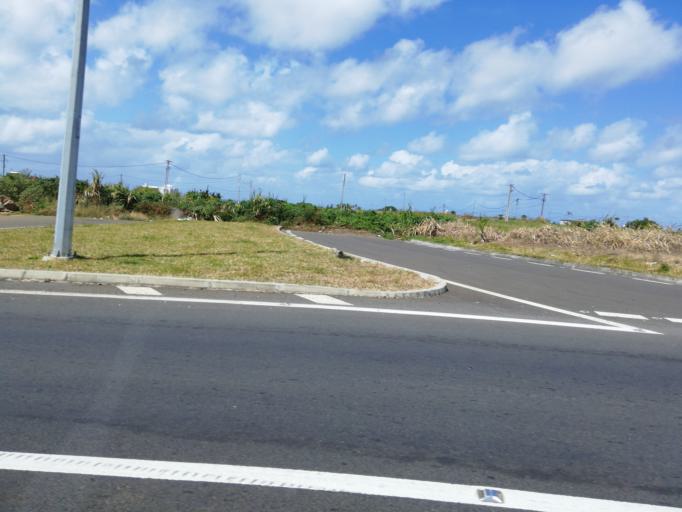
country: MU
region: Grand Port
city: Plaine Magnien
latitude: -20.4421
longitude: 57.6686
